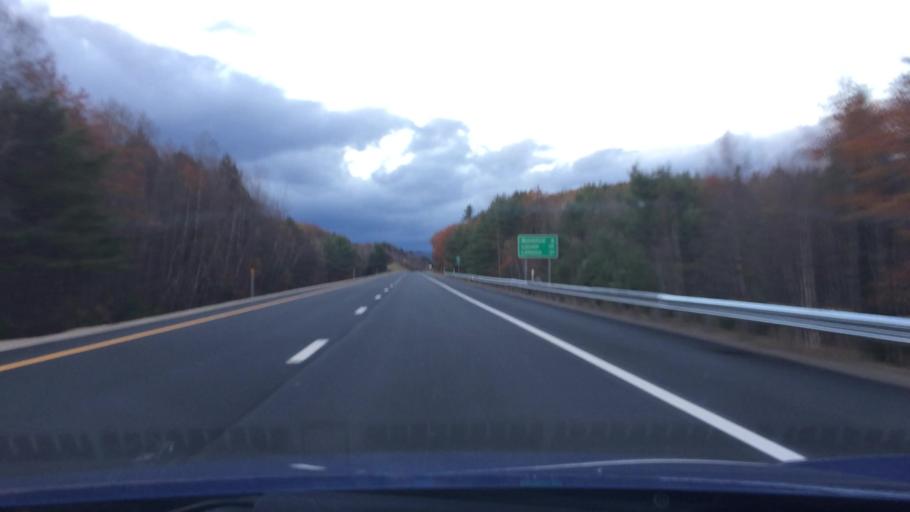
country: US
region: New Hampshire
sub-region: Grafton County
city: Thornton
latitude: 43.8818
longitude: -71.6768
